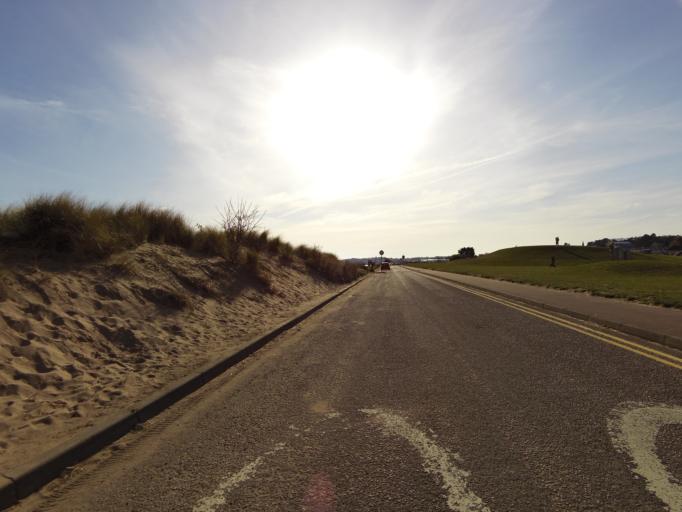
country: GB
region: Scotland
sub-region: Fife
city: Tayport
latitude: 56.4789
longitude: -2.8128
